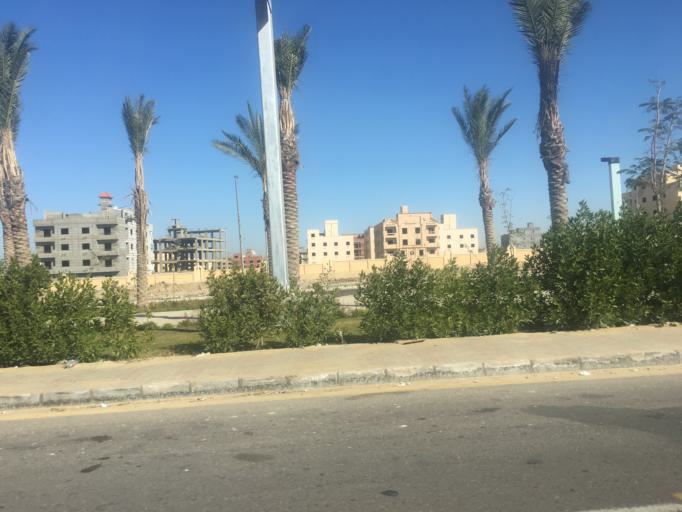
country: EG
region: Al Jizah
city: Awsim
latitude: 30.0149
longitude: 30.9767
